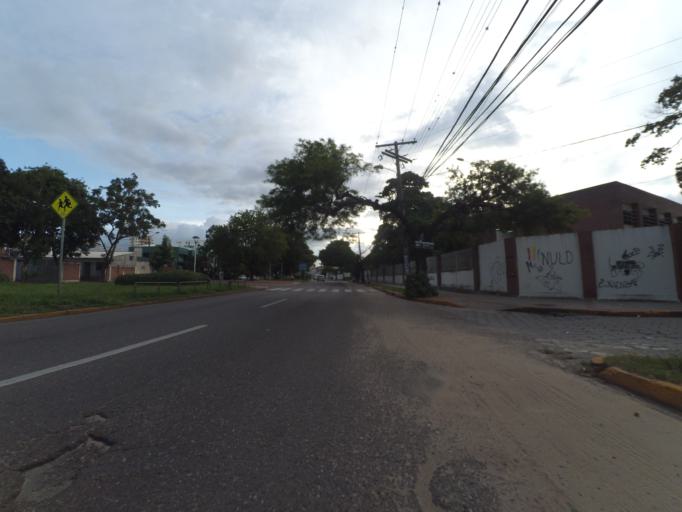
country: BO
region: Santa Cruz
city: Santa Cruz de la Sierra
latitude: -17.7767
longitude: -63.1872
